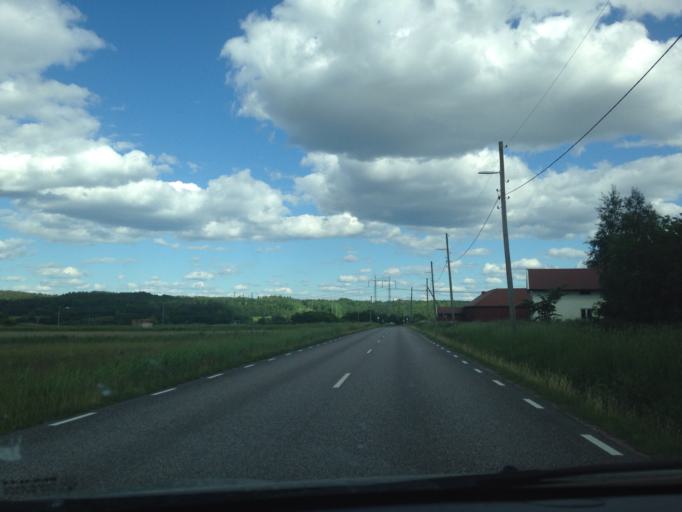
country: SE
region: Vaestra Goetaland
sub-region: Goteborg
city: Goeteborg
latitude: 57.7713
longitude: 11.9262
